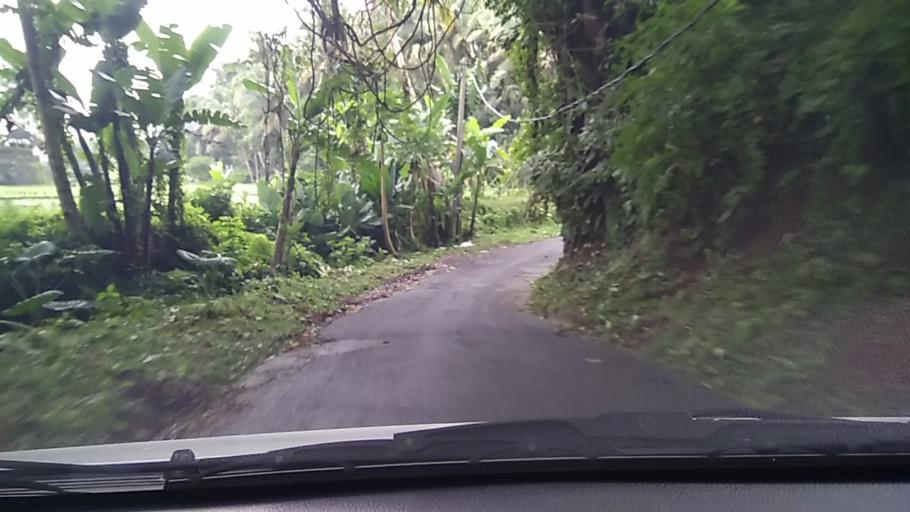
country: ID
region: Bali
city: Banjar Dujung Kaja
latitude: -8.4077
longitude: 115.2888
